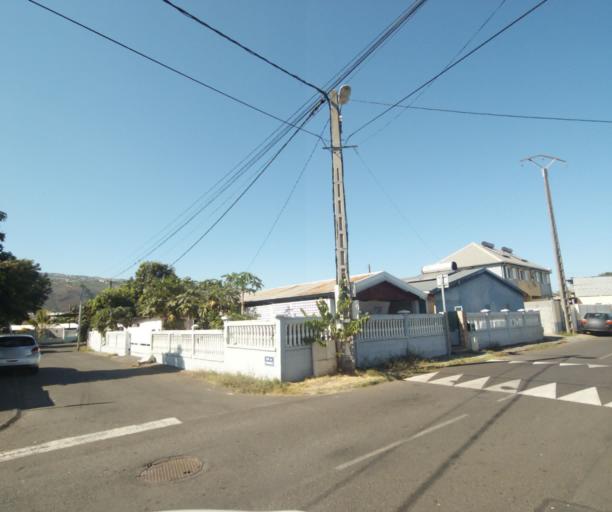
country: RE
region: Reunion
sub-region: Reunion
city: Saint-Paul
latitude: -20.9849
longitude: 55.2957
